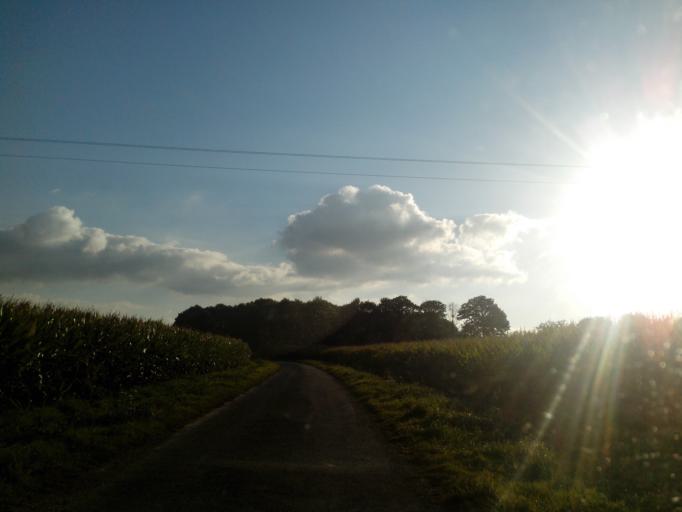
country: FR
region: Brittany
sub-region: Departement du Morbihan
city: Mauron
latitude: 48.1054
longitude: -2.3562
